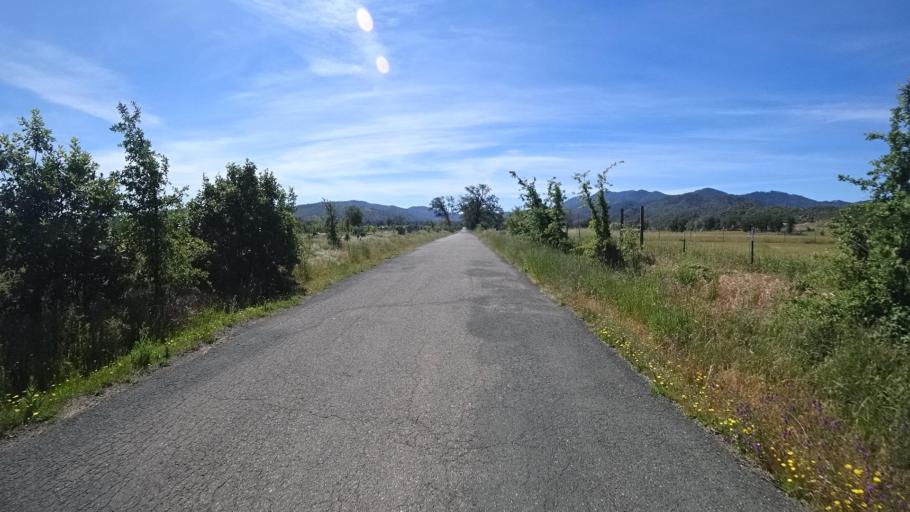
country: US
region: California
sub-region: Lake County
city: Middletown
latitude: 38.7560
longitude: -122.6399
